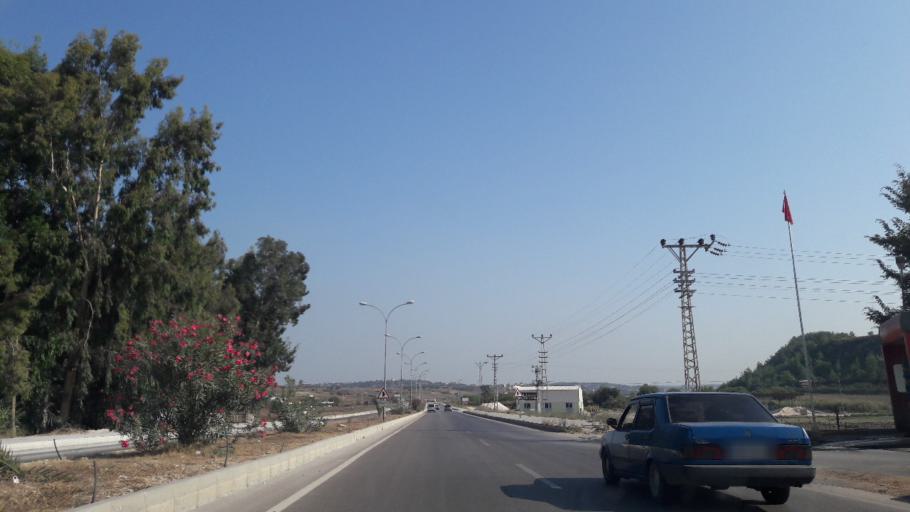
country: TR
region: Adana
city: Yuregir
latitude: 37.0556
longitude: 35.4417
